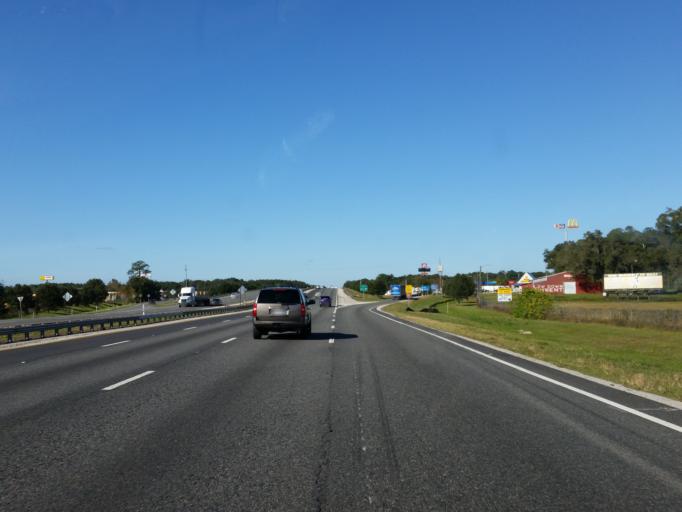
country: US
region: Florida
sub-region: Marion County
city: Ocala
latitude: 29.2626
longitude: -82.1913
